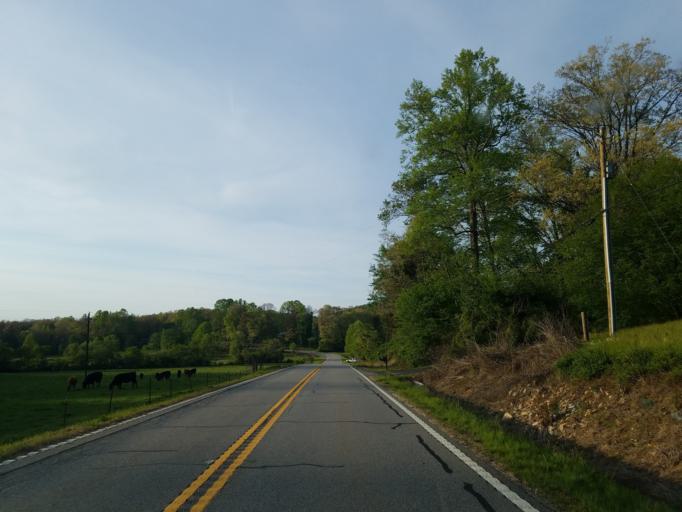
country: US
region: Georgia
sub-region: Fannin County
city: Blue Ridge
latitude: 34.8348
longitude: -84.1902
